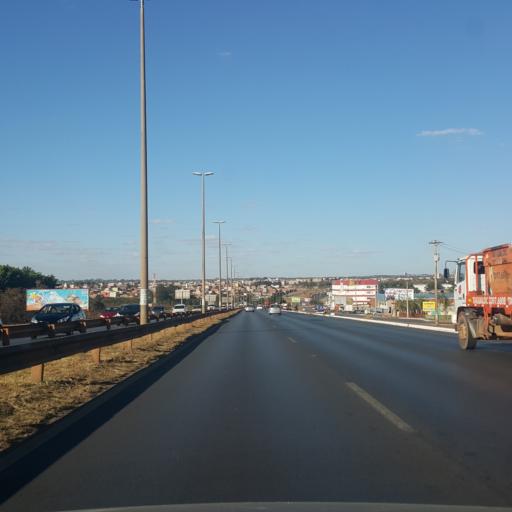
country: BR
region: Federal District
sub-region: Brasilia
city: Brasilia
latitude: -15.7881
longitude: -48.0135
